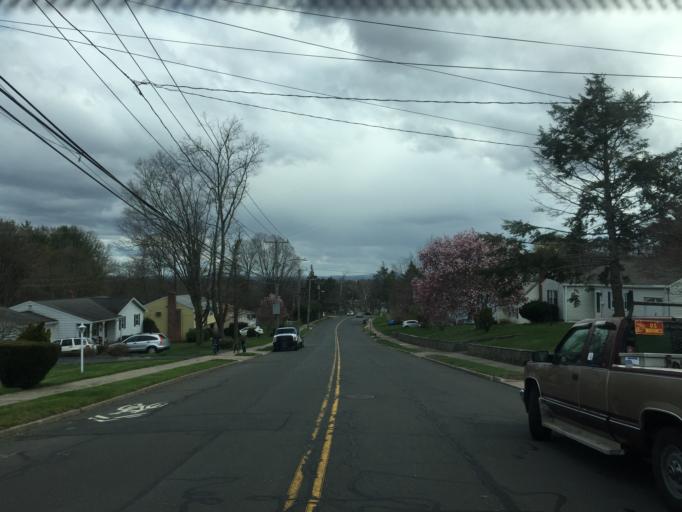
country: US
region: Connecticut
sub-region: Hartford County
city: New Britain
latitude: 41.7102
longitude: -72.7766
